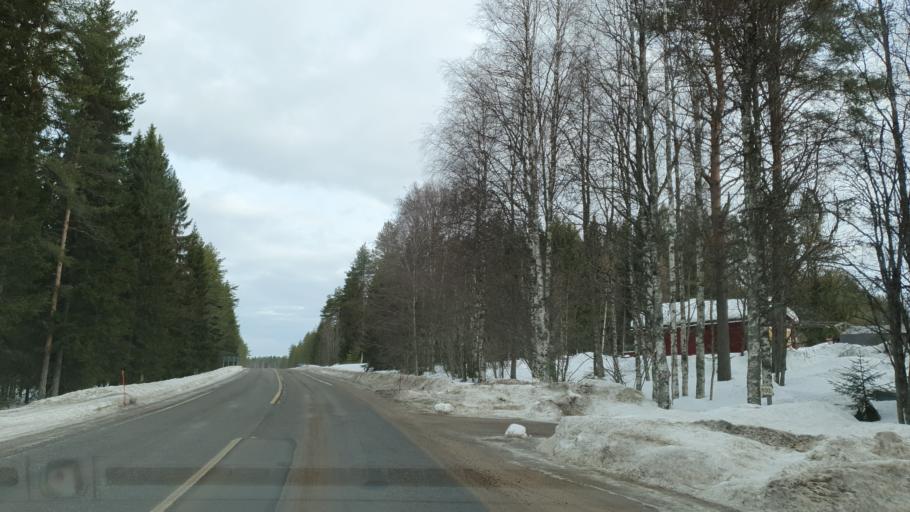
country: FI
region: Kainuu
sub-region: Kajaani
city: Vuokatti
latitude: 64.2264
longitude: 28.0677
